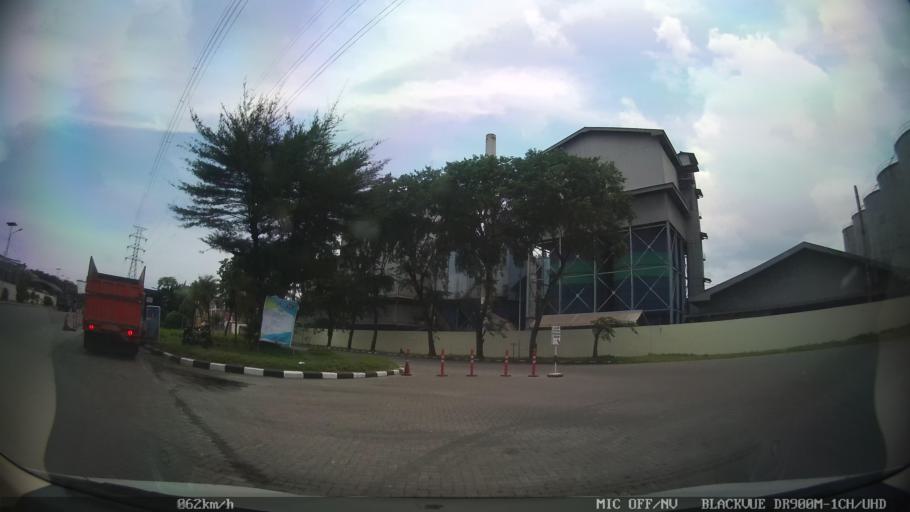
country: ID
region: North Sumatra
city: Labuhan Deli
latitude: 3.6732
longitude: 98.6851
